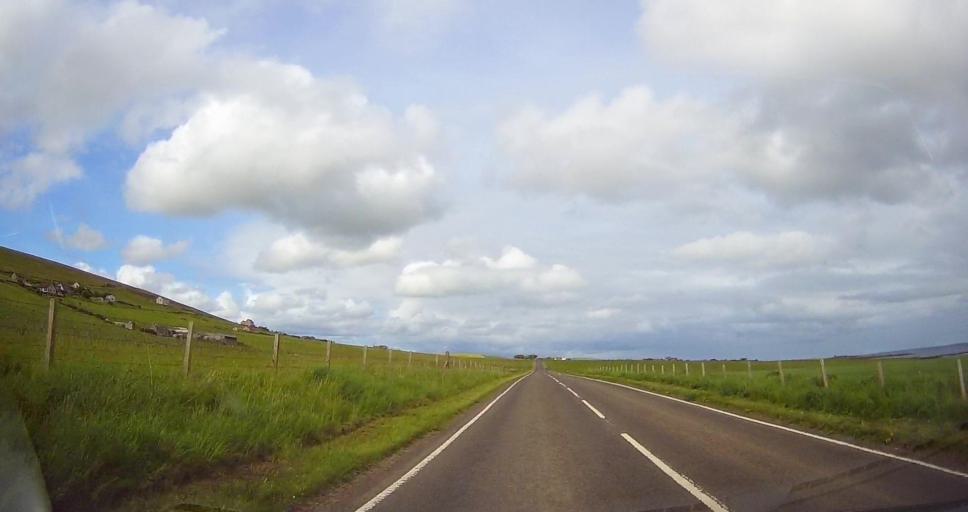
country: GB
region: Scotland
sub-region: Orkney Islands
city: Orkney
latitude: 59.0143
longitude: -3.1081
